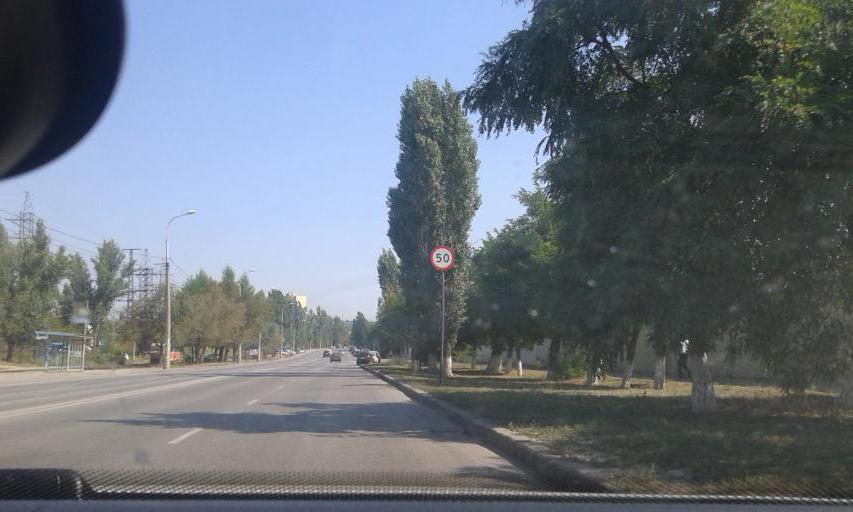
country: RU
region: Volgograd
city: Volgograd
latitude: 48.6522
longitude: 44.4430
